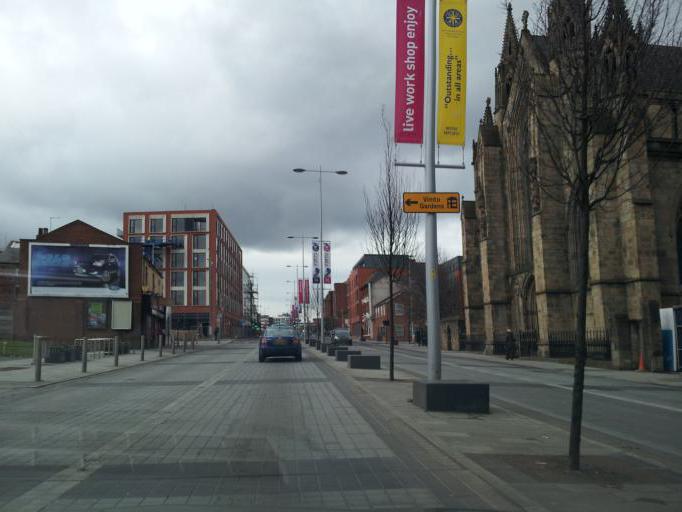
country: GB
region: England
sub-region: Manchester
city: Hulme
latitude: 53.4834
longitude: -2.2606
